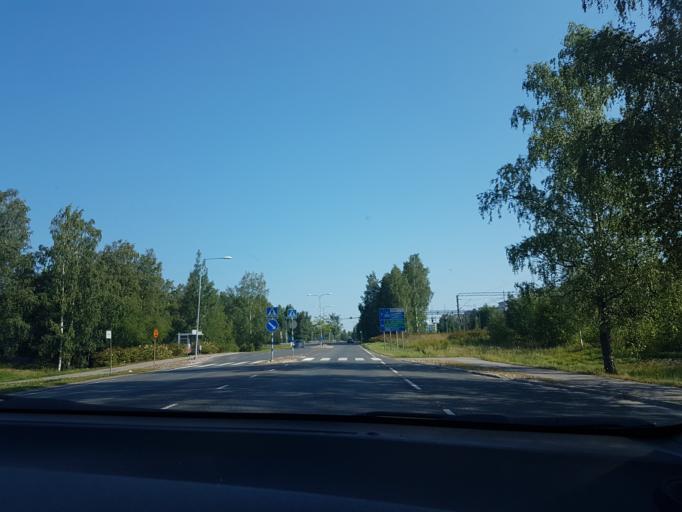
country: FI
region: Uusimaa
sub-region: Helsinki
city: Kerava
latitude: 60.3926
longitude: 25.1013
